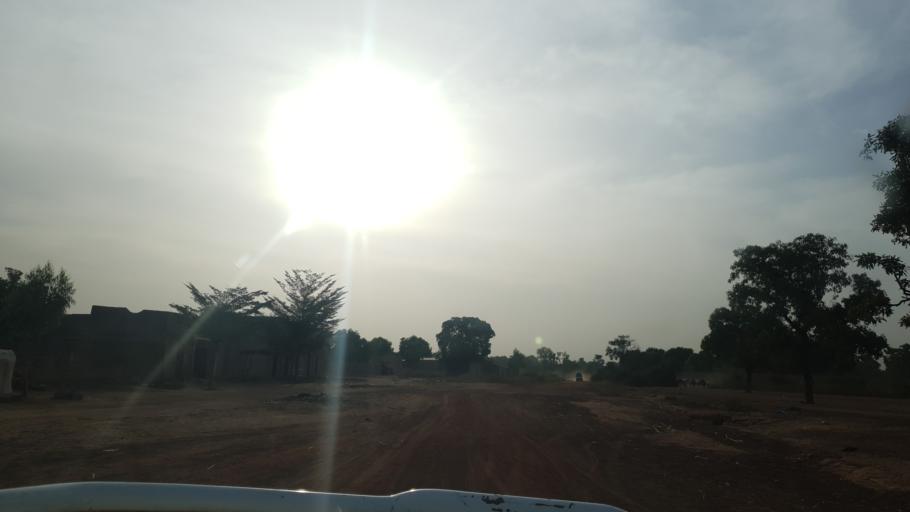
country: ML
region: Segou
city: Baroueli
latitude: 12.7728
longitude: -6.9359
